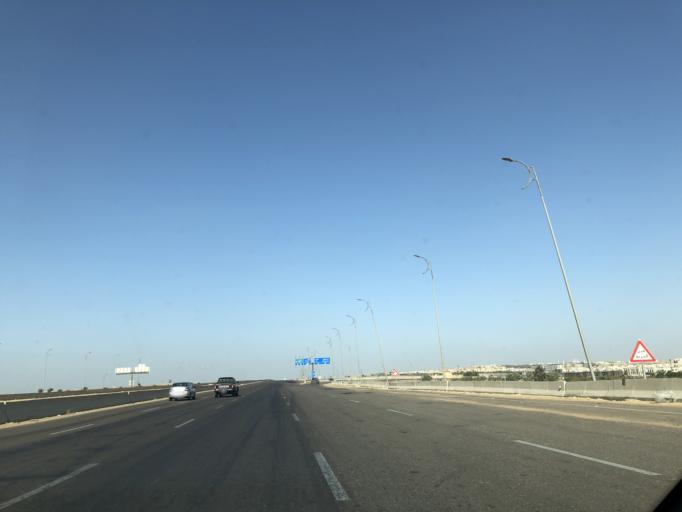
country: EG
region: Al Jizah
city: Awsim
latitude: 30.0732
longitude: 30.9201
